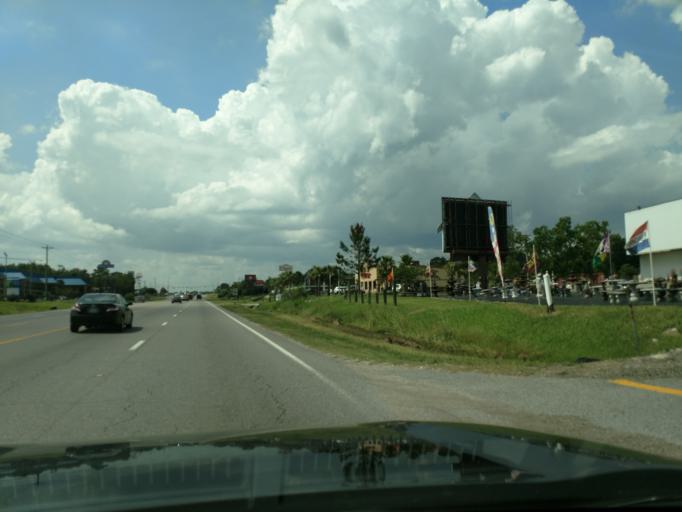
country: US
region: Mississippi
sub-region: Jackson County
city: Gulf Hills
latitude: 30.4461
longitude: -88.8399
